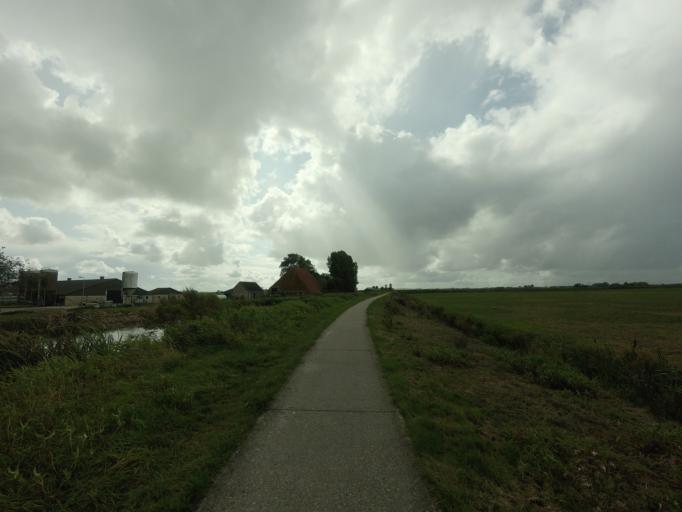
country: NL
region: Friesland
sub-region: Gemeente Boarnsterhim
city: Wergea
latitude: 53.1447
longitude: 5.8244
